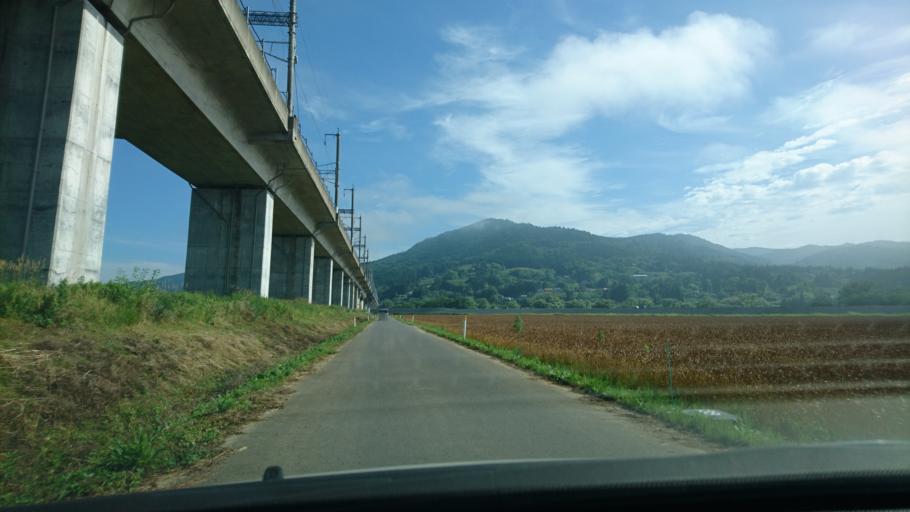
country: JP
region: Iwate
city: Ichinoseki
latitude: 38.9685
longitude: 141.1542
